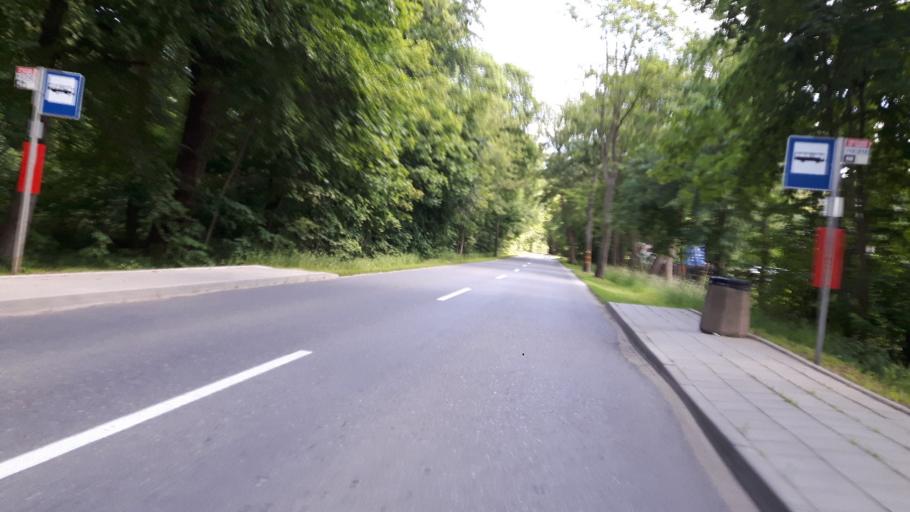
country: PL
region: Pomeranian Voivodeship
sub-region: Powiat gdanski
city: Cedry Wielkie
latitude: 54.3424
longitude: 18.8582
